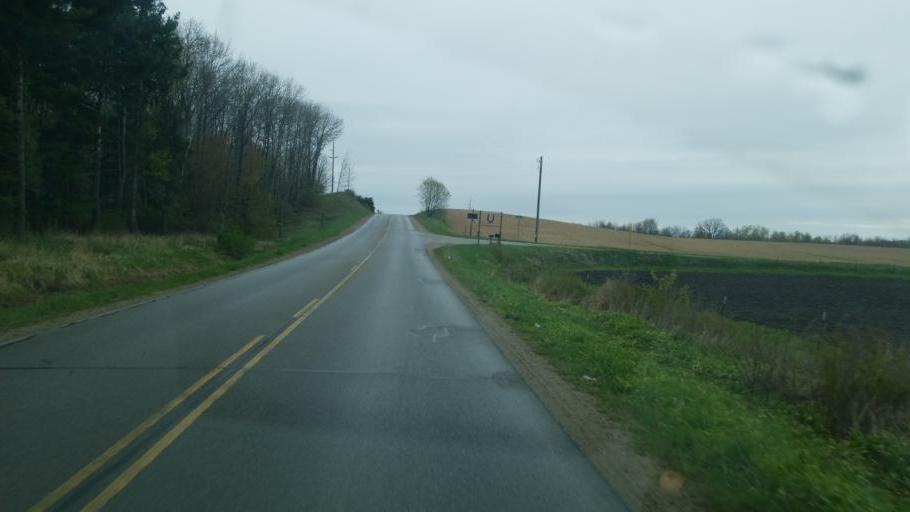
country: US
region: Michigan
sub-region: Montcalm County
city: Lakeview
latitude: 43.4958
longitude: -85.2541
